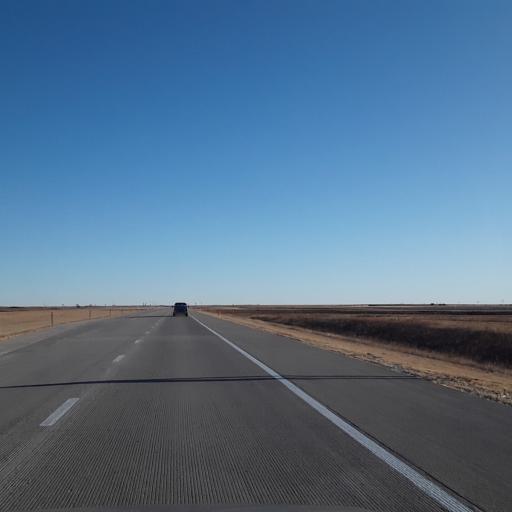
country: US
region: Kansas
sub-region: Seward County
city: Liberal
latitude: 37.1014
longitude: -100.7995
